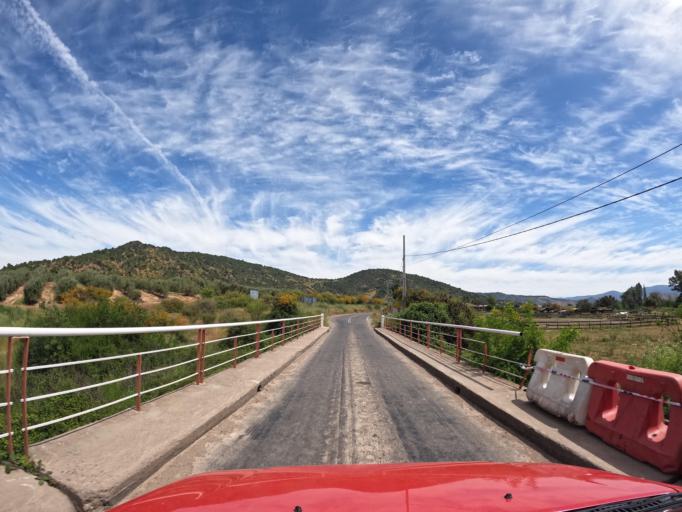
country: CL
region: Maule
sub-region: Provincia de Talca
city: Talca
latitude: -35.1191
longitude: -71.6458
